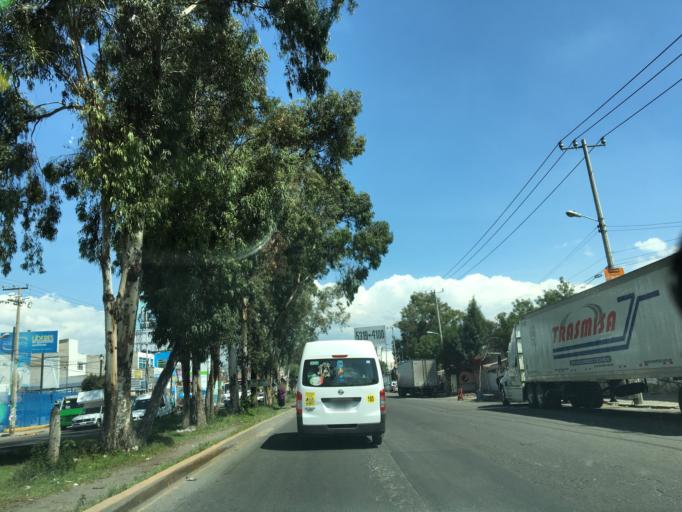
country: MX
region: Mexico
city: Los Reyes La Paz
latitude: 19.3562
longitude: -98.9832
